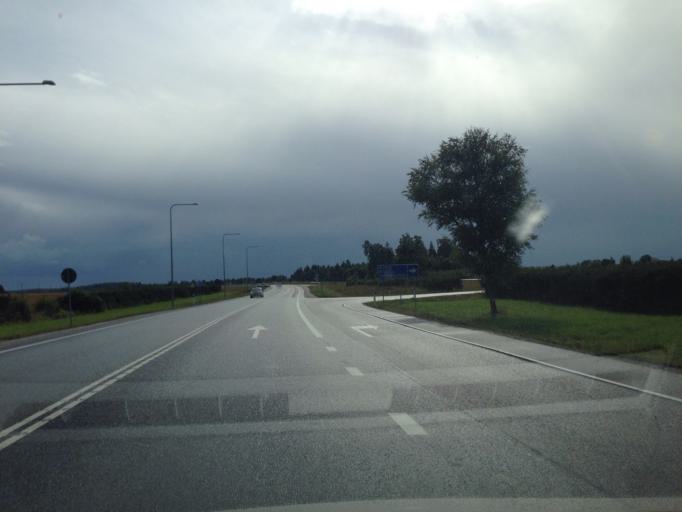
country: EE
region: Jaervamaa
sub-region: Paide linn
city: Paide
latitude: 58.9410
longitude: 25.6120
